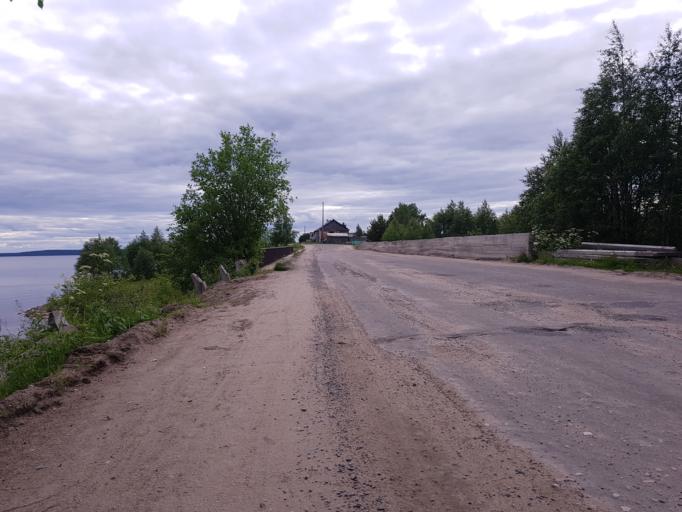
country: RU
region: Republic of Karelia
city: Kalevala
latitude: 65.1925
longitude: 31.1723
